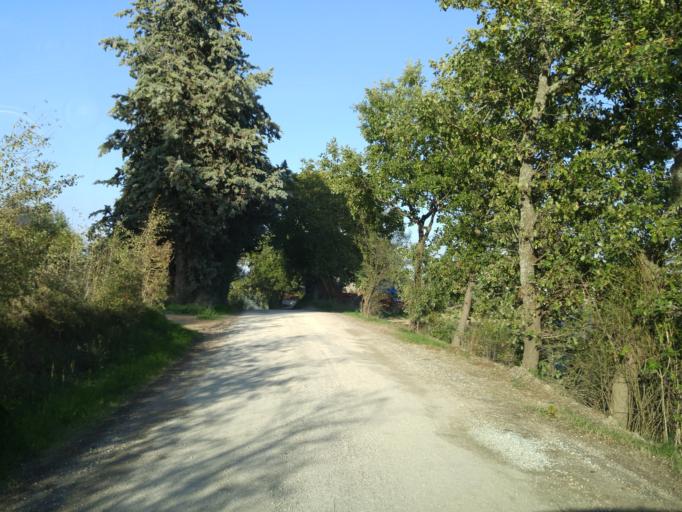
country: IT
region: The Marches
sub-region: Provincia di Pesaro e Urbino
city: Fossombrone
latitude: 43.7151
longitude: 12.8165
